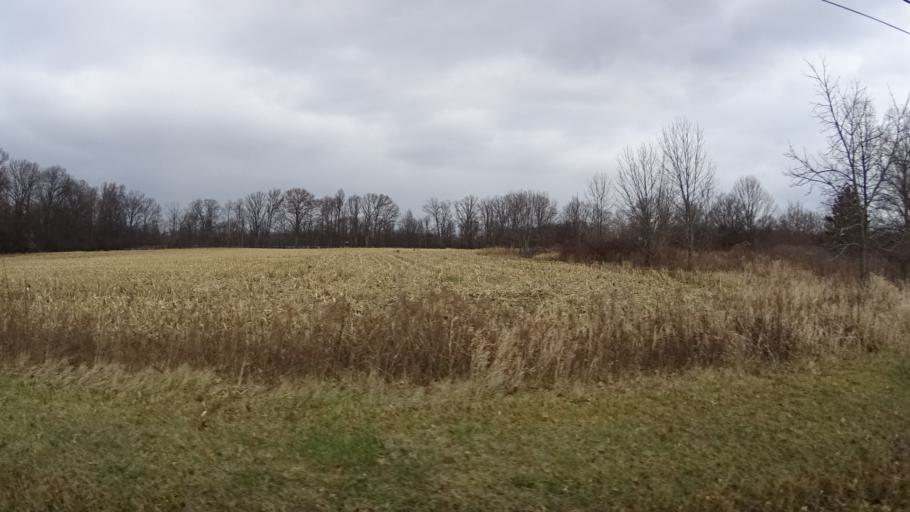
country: US
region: Ohio
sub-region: Lorain County
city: Oberlin
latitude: 41.2828
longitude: -82.1945
